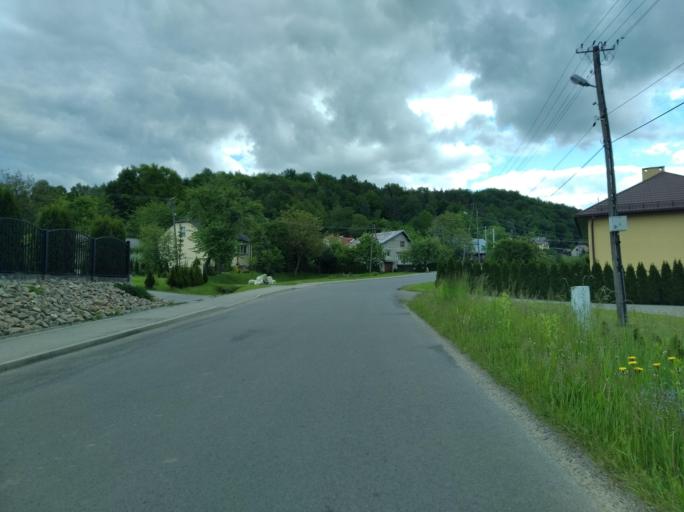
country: PL
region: Subcarpathian Voivodeship
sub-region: Powiat brzozowski
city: Jablonica Polska
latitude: 49.6962
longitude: 21.9300
